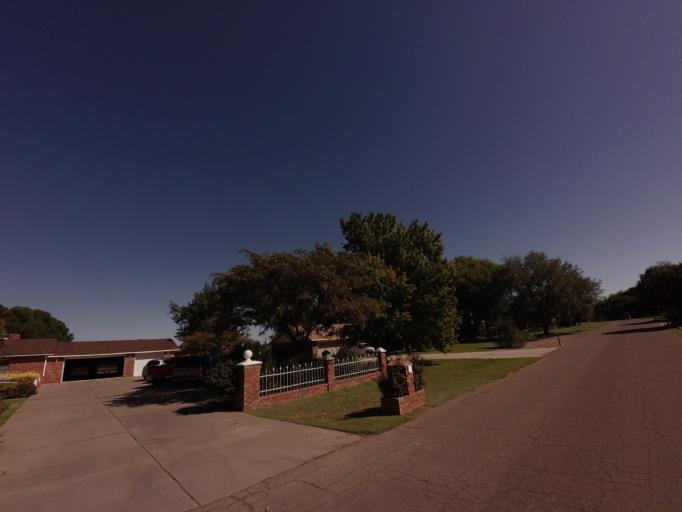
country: US
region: New Mexico
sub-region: Curry County
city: Clovis
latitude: 34.4276
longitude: -103.1707
